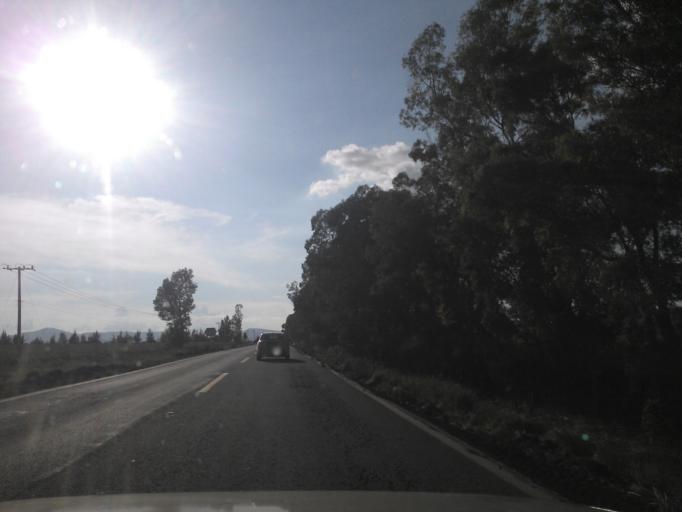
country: MX
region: Jalisco
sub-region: Tototlan
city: Nuevo Refugio de Afuera (Nuevo Refugio)
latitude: 20.5515
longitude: -102.6777
